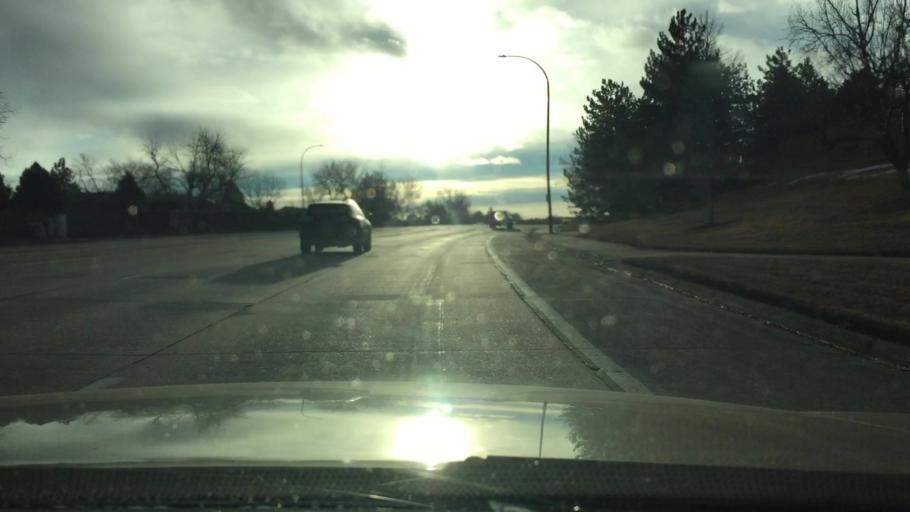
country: US
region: Colorado
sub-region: Douglas County
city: Highlands Ranch
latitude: 39.5457
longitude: -104.9747
